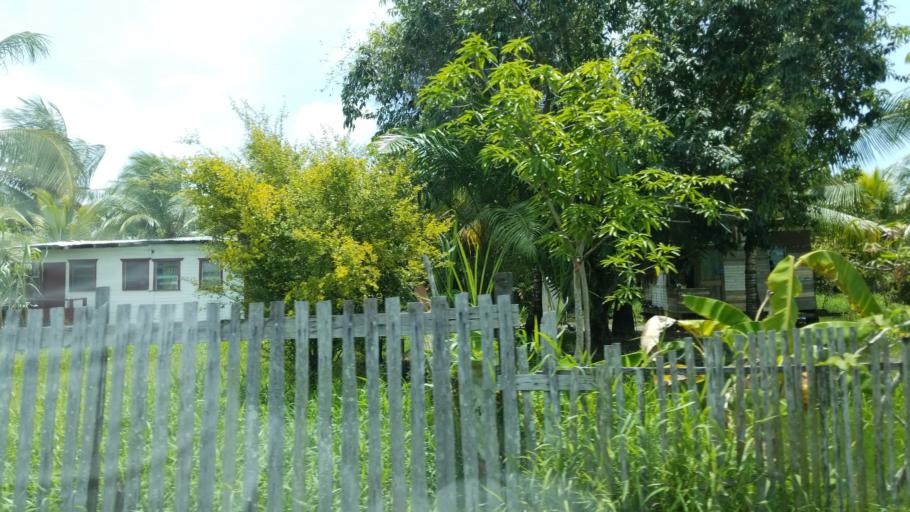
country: GY
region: Demerara-Mahaica
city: Georgetown
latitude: 6.7917
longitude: -58.1216
